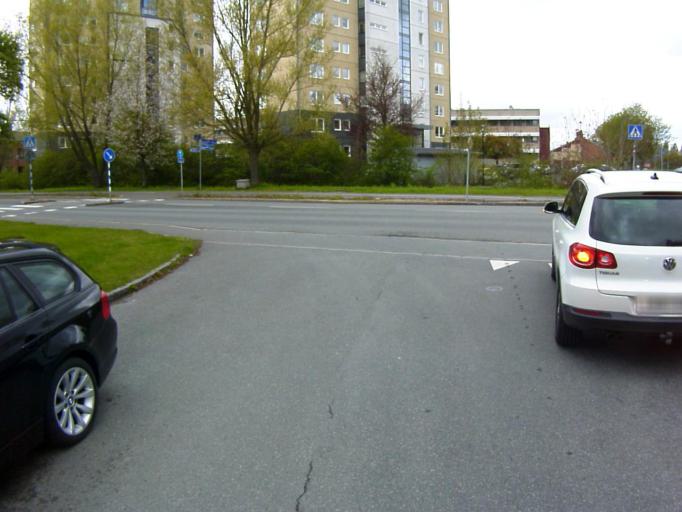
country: SE
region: Skane
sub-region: Kristianstads Kommun
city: Kristianstad
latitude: 56.0384
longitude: 14.1614
